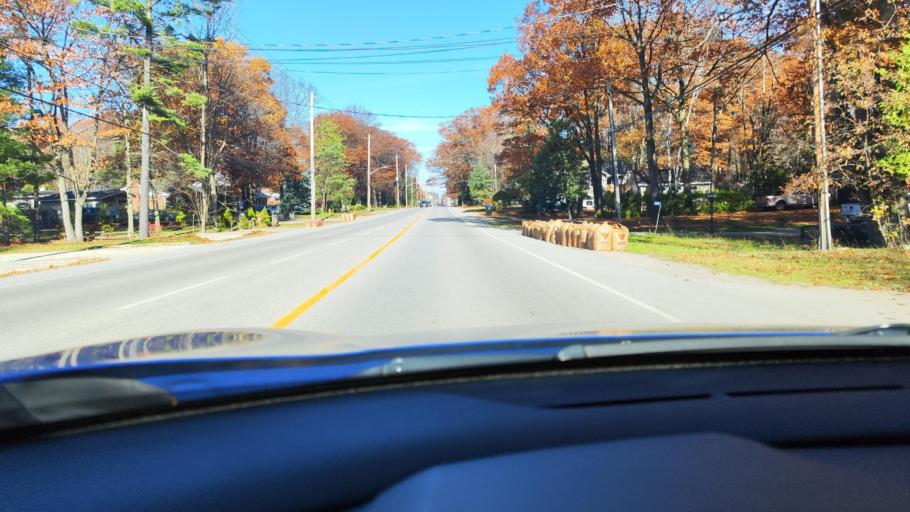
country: CA
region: Ontario
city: Wasaga Beach
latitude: 44.4646
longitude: -80.0738
